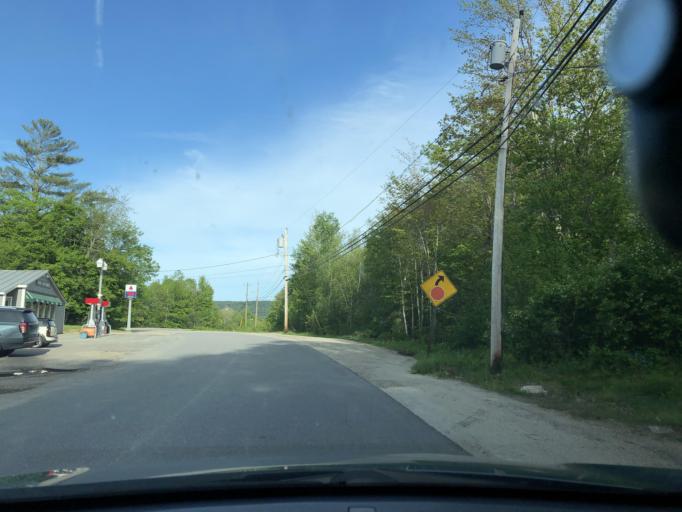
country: US
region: New Hampshire
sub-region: Merrimack County
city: Wilmot
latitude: 43.4178
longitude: -71.9328
